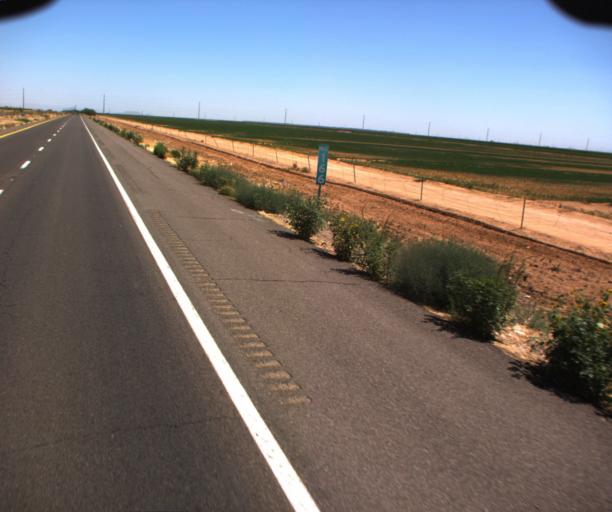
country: US
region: Arizona
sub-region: Pinal County
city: Maricopa
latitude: 32.9490
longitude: -112.0480
